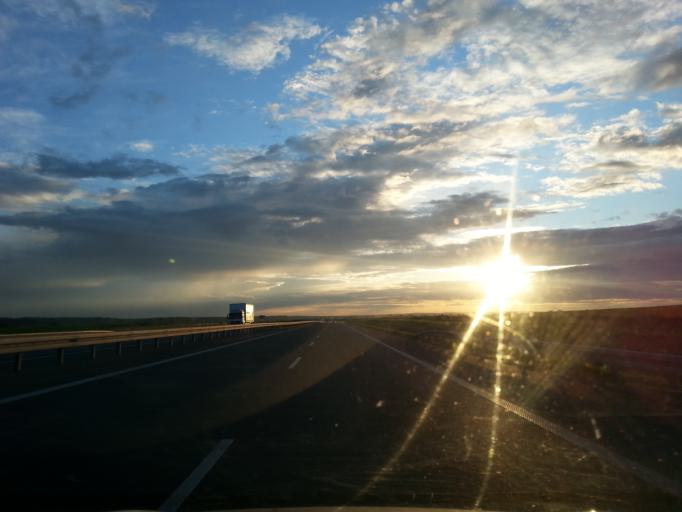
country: PL
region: Lower Silesian Voivodeship
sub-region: Powiat olesnicki
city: Sycow
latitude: 51.2975
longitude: 17.6627
